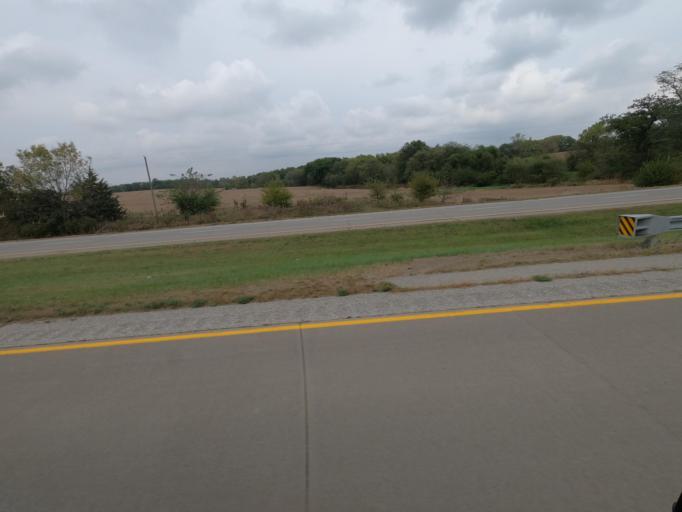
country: US
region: Iowa
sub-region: Wapello County
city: Eddyville
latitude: 41.1204
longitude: -92.5553
